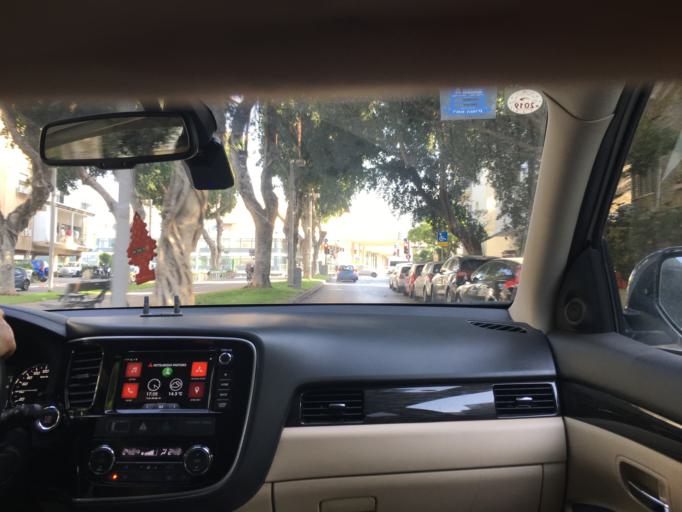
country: IL
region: Tel Aviv
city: Tel Aviv
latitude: 32.0747
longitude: 34.7798
